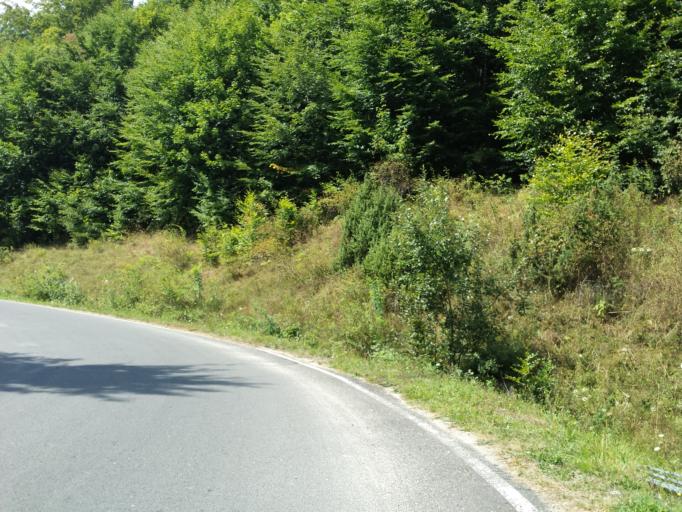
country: PL
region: Subcarpathian Voivodeship
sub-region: Powiat bieszczadzki
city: Lutowiska
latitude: 49.1430
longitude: 22.5515
